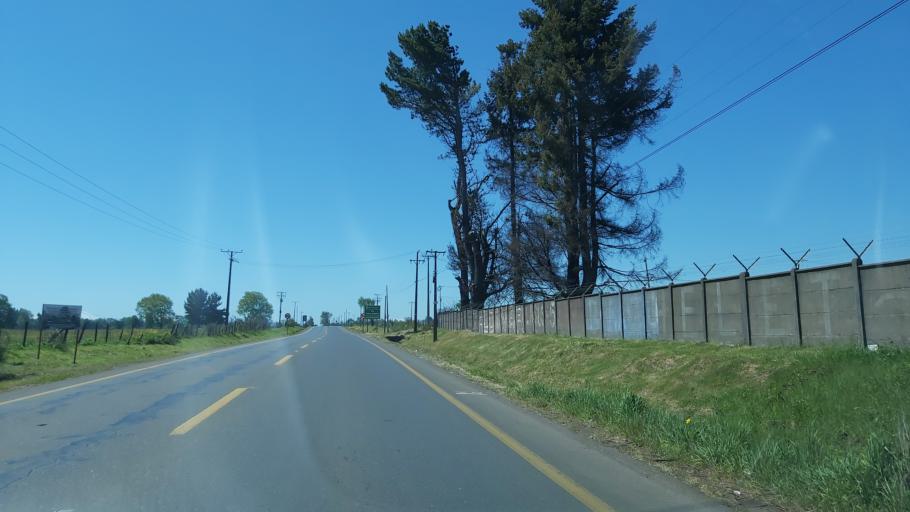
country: CL
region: Araucania
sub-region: Provincia de Malleco
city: Victoria
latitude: -38.2453
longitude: -72.3150
